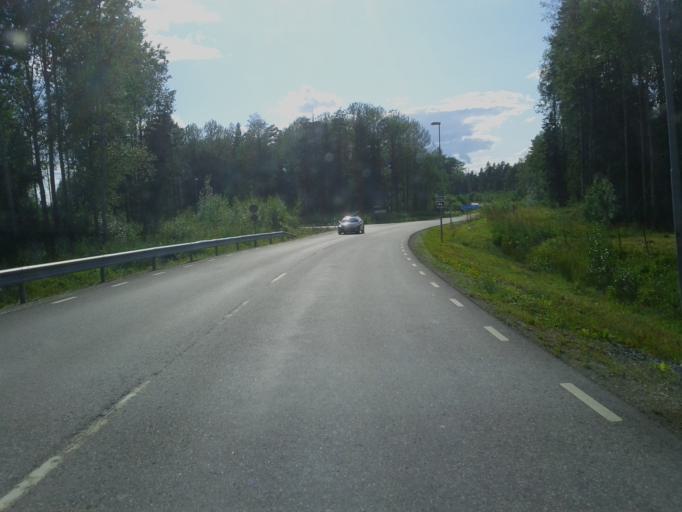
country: SE
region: Vaestmanland
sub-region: Sala Kommun
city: Sala
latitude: 59.9100
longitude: 16.5543
